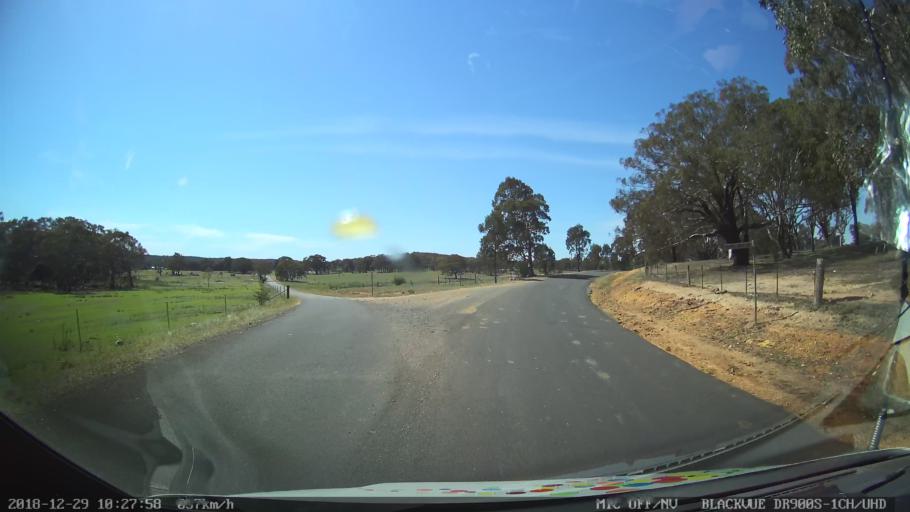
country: AU
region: New South Wales
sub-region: Yass Valley
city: Gundaroo
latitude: -34.9388
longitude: 149.4532
